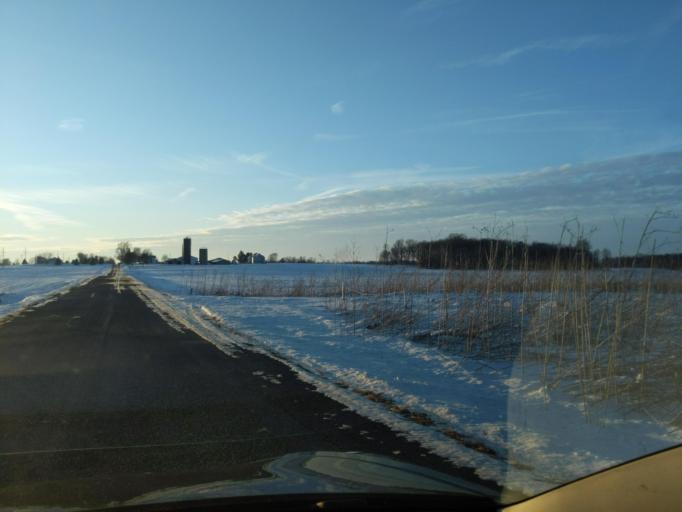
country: US
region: Michigan
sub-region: Ingham County
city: Webberville
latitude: 42.5694
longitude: -84.1820
